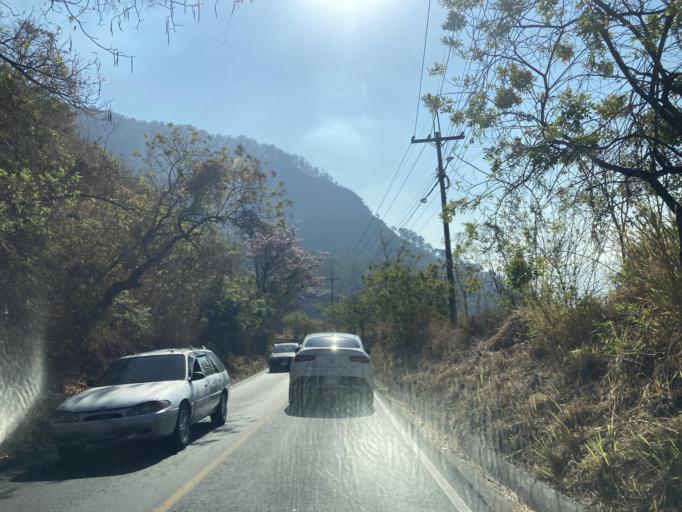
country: GT
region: Guatemala
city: Amatitlan
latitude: 14.4952
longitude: -90.6234
